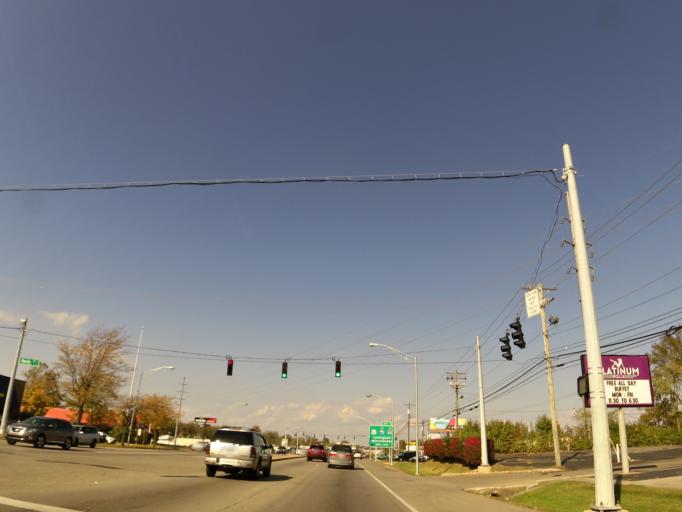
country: US
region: Kentucky
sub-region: Fayette County
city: Lexington-Fayette
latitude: 38.0347
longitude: -84.4536
